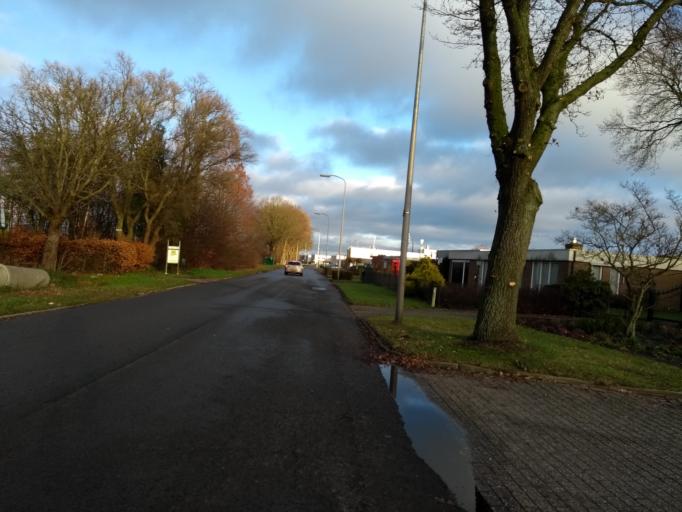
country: NL
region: Overijssel
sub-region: Gemeente Almelo
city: Almelo
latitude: 52.3764
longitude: 6.6416
